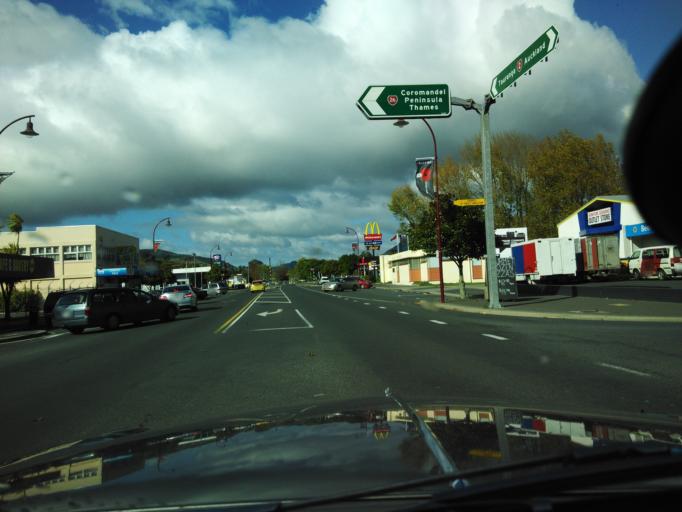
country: NZ
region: Waikato
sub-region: Hauraki District
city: Paeroa
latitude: -37.3817
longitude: 175.6725
